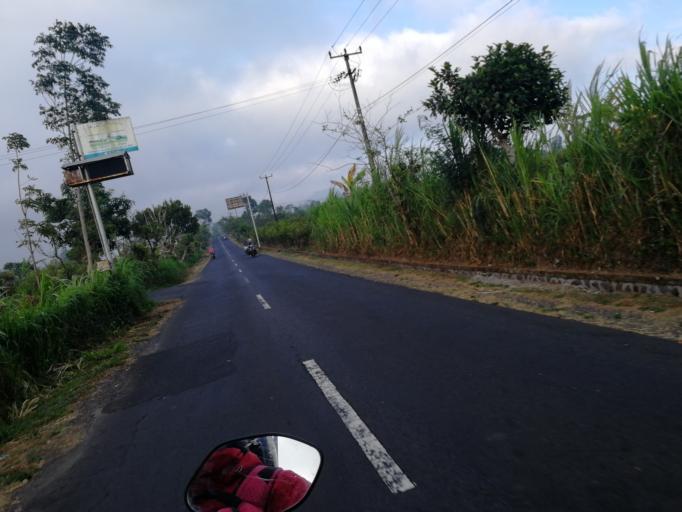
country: ID
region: Bali
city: Banjar Kedisan
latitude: -8.2234
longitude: 115.2594
